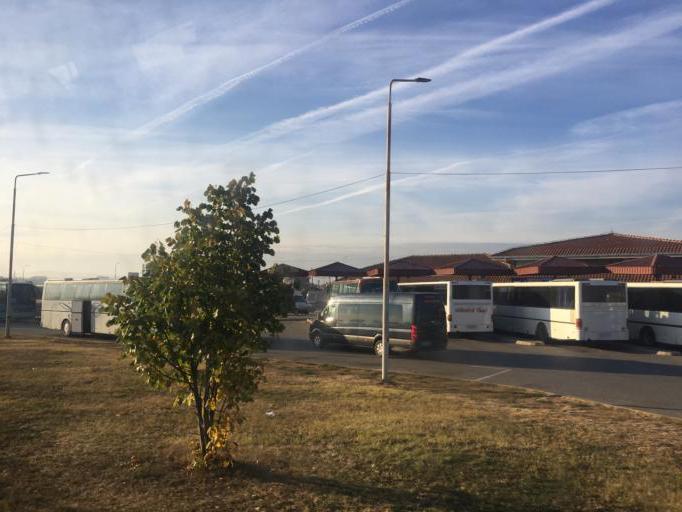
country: XK
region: Pristina
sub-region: Komuna e Drenasit
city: Glogovac
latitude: 42.6213
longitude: 20.8932
